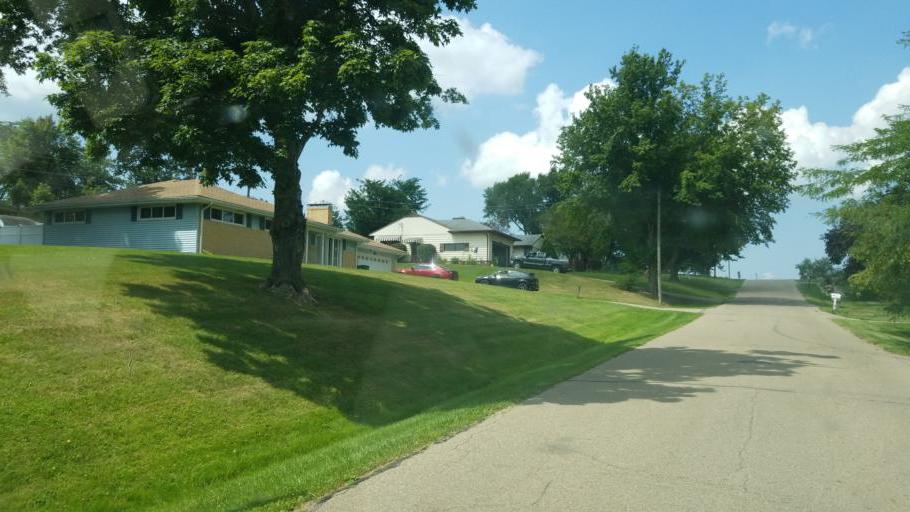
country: US
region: Ohio
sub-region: Knox County
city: Mount Vernon
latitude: 40.3996
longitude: -82.4651
